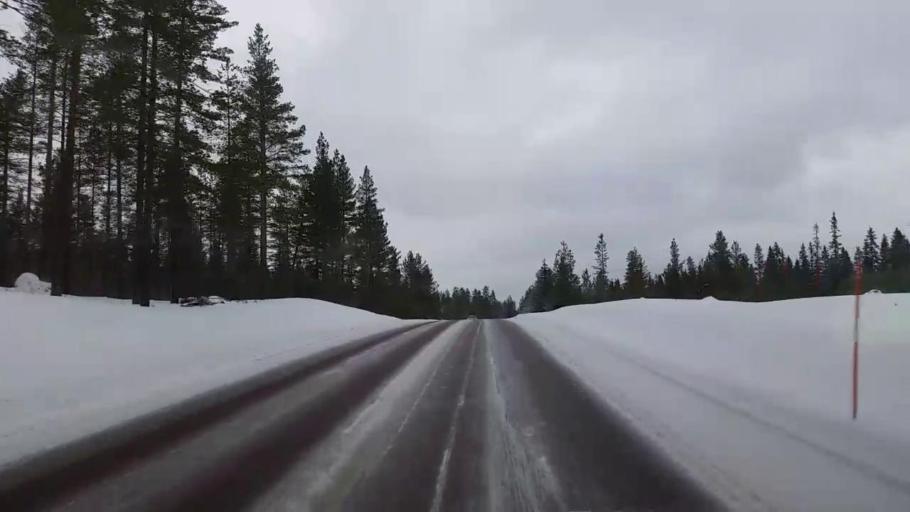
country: SE
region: Jaemtland
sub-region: Bergs Kommun
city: Hoverberg
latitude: 62.4256
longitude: 14.6014
